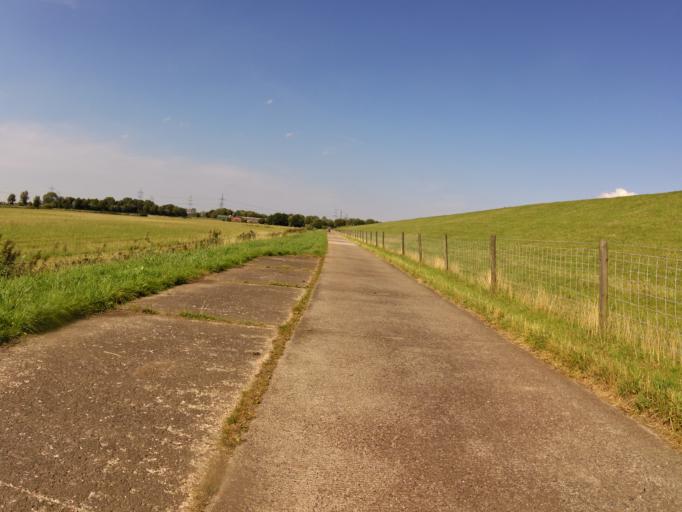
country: DE
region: Lower Saxony
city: Nordenham
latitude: 53.4194
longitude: 8.4725
